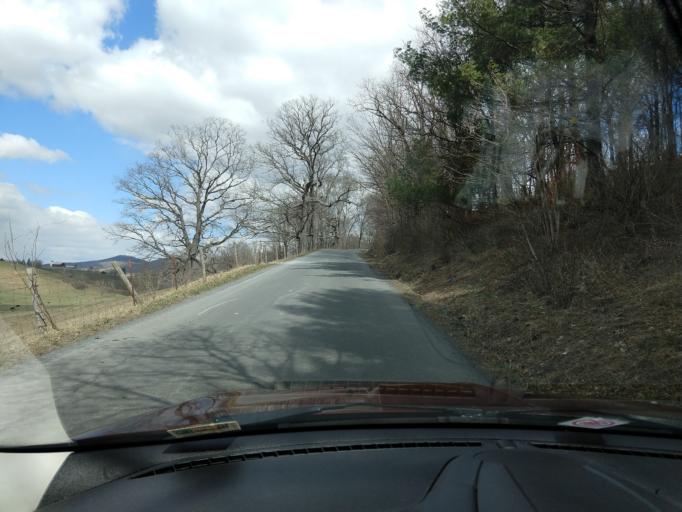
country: US
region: West Virginia
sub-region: Greenbrier County
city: Lewisburg
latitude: 37.8109
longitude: -80.4866
